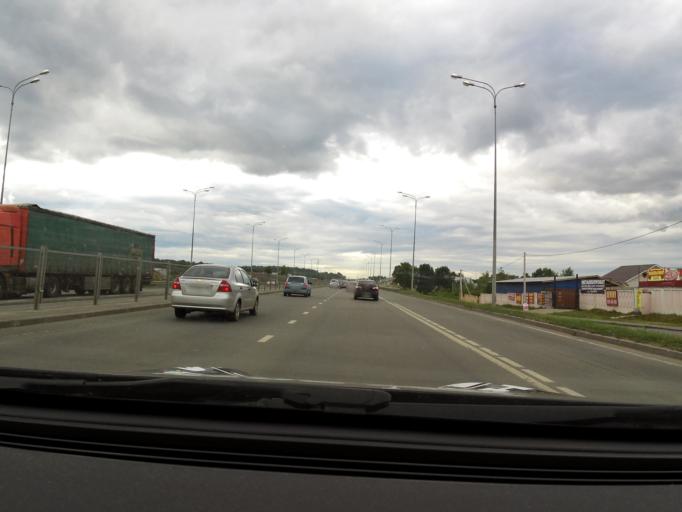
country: RU
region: Tatarstan
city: Osinovo
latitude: 55.8517
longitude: 48.8862
